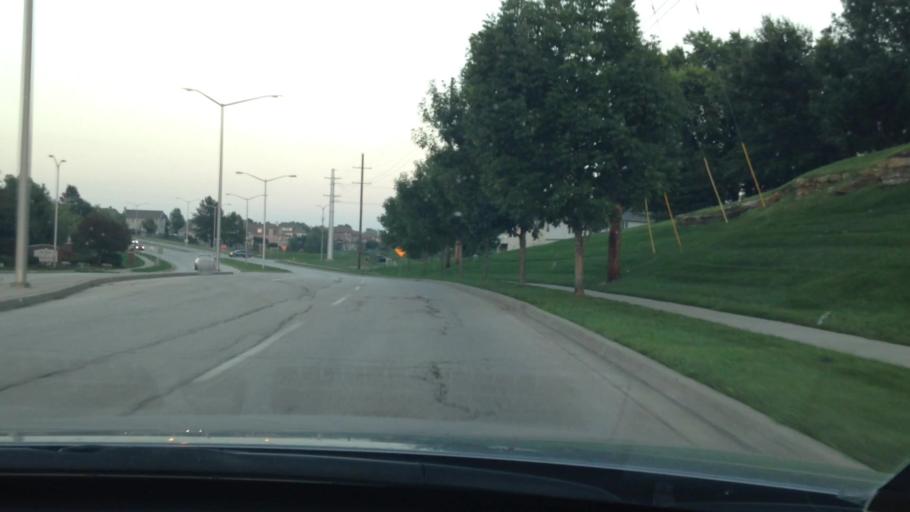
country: US
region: Missouri
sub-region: Clay County
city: Pleasant Valley
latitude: 39.2668
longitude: -94.4684
